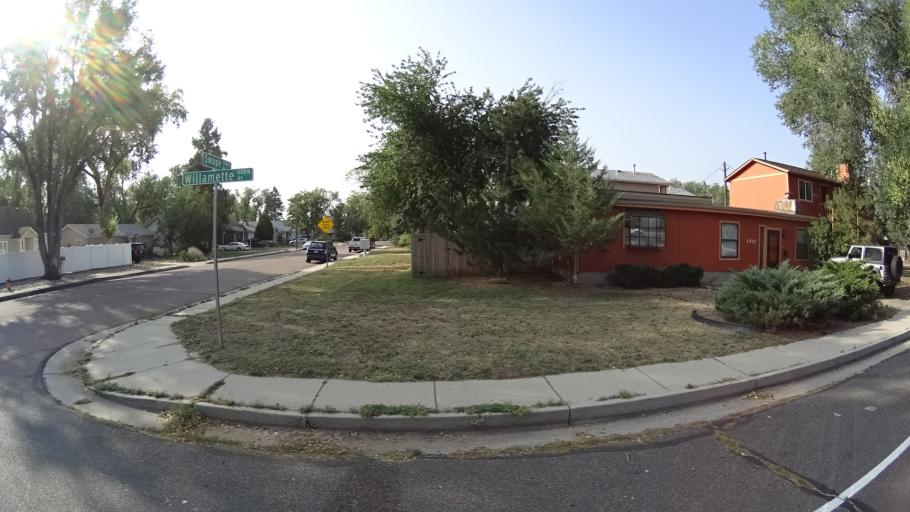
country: US
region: Colorado
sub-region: El Paso County
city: Colorado Springs
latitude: 38.8409
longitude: -104.7917
